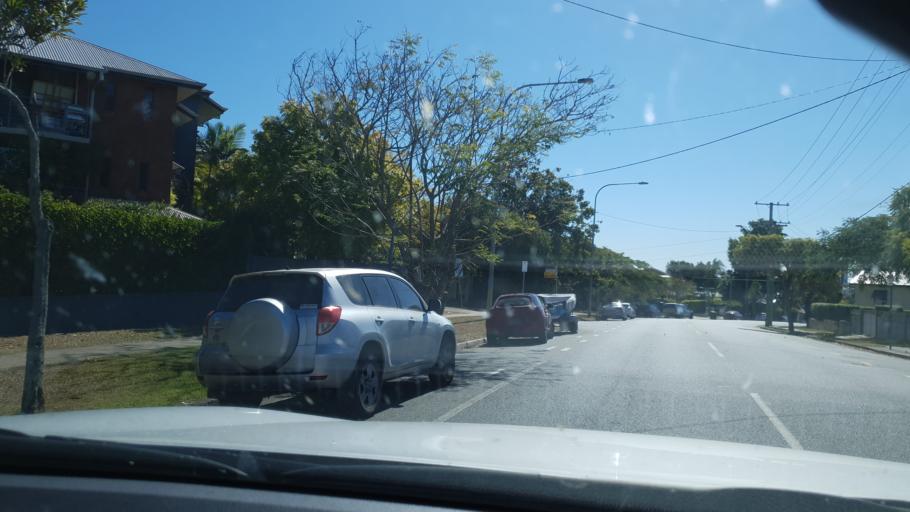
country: AU
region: Queensland
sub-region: Brisbane
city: Annerley
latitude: -27.5080
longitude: 153.0324
